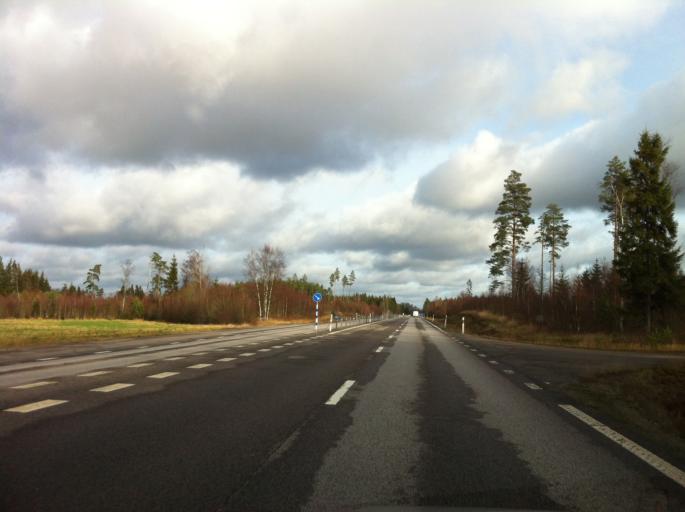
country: SE
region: Kronoberg
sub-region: Alvesta Kommun
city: Vislanda
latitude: 56.7168
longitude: 14.4535
